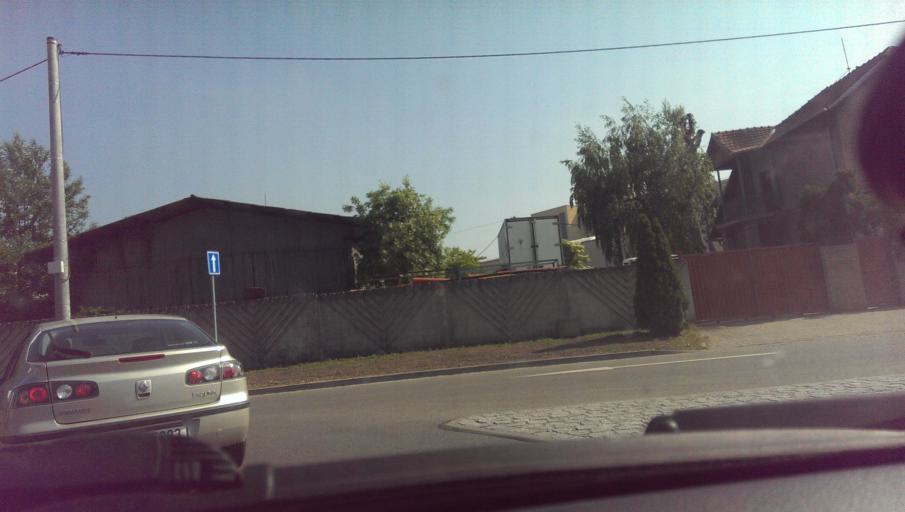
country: CZ
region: Zlin
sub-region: Okres Uherske Hradiste
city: Stare Mesto
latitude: 49.0757
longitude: 17.4245
